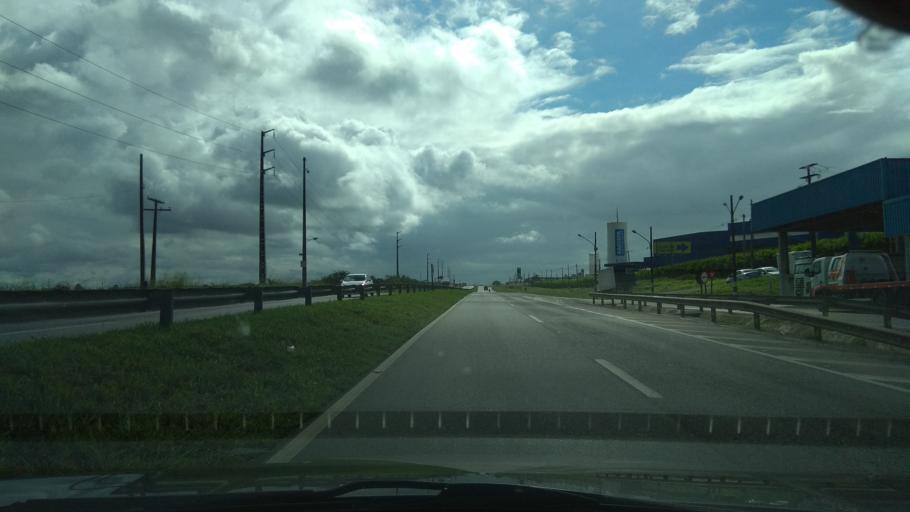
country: BR
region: Bahia
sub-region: Conceicao Do Jacuipe
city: Conceicao do Jacuipe
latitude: -12.3442
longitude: -38.8407
